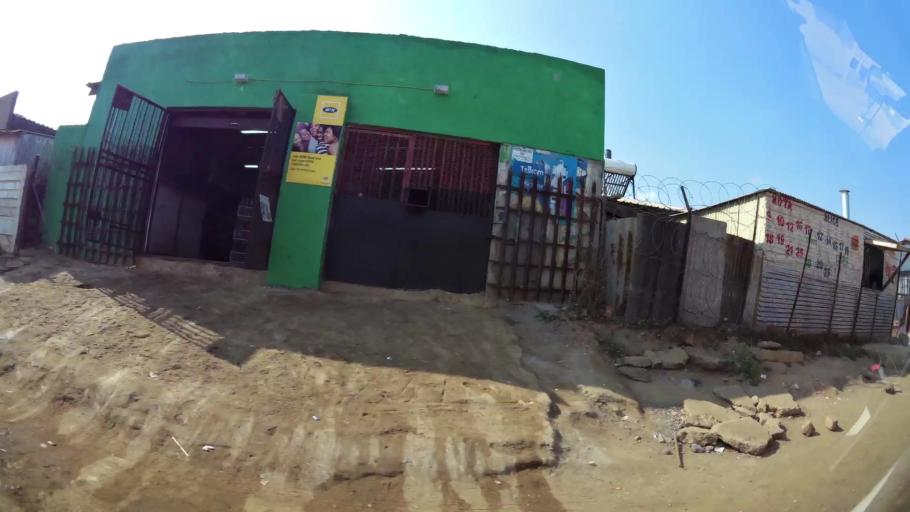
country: ZA
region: Gauteng
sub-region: Ekurhuleni Metropolitan Municipality
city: Springs
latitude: -26.1118
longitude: 28.4854
